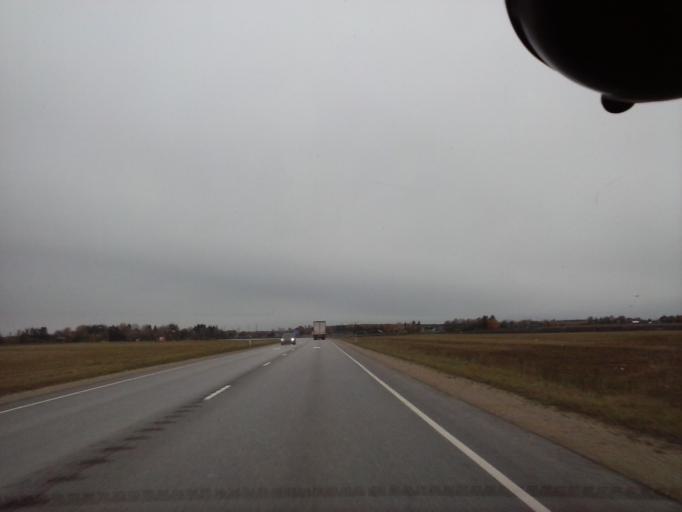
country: EE
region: Jogevamaa
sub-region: Poltsamaa linn
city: Poltsamaa
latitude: 58.6688
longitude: 25.9725
